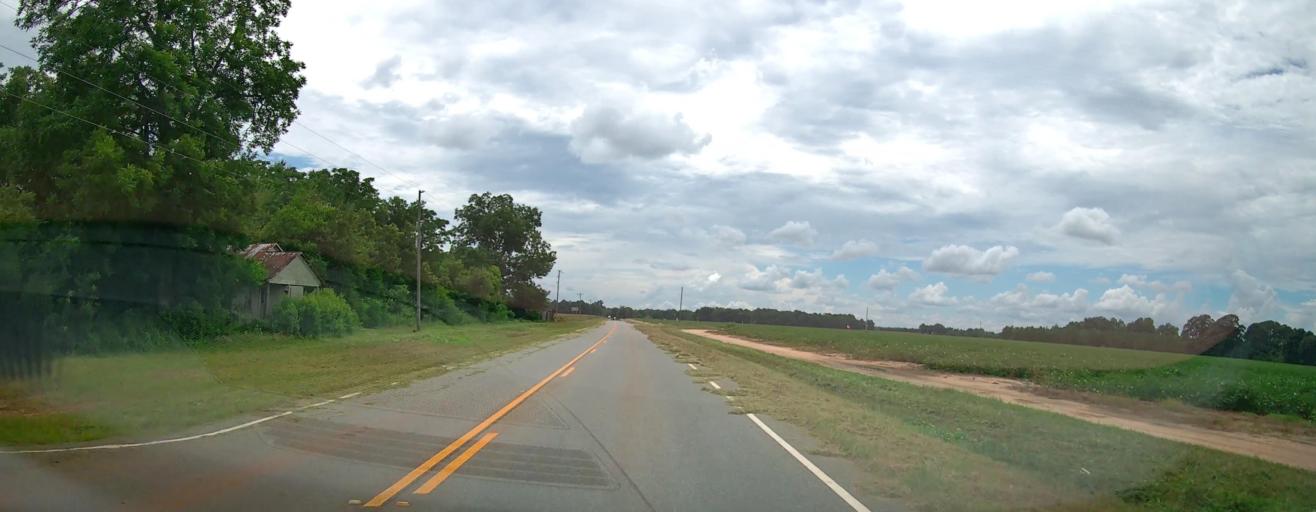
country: US
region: Georgia
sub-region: Macon County
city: Oglethorpe
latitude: 32.2803
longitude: -84.1738
